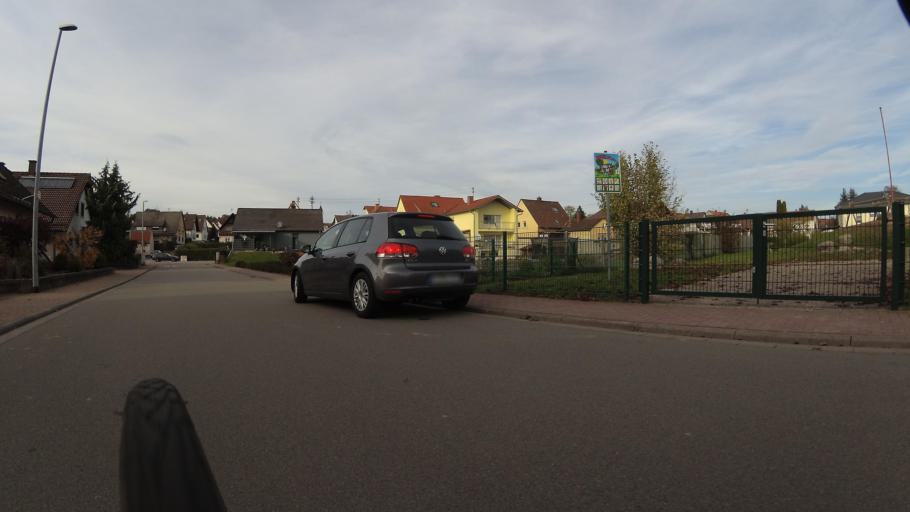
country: DE
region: Rheinland-Pfalz
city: Ramstein-Miesenbach
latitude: 49.4565
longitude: 7.5560
